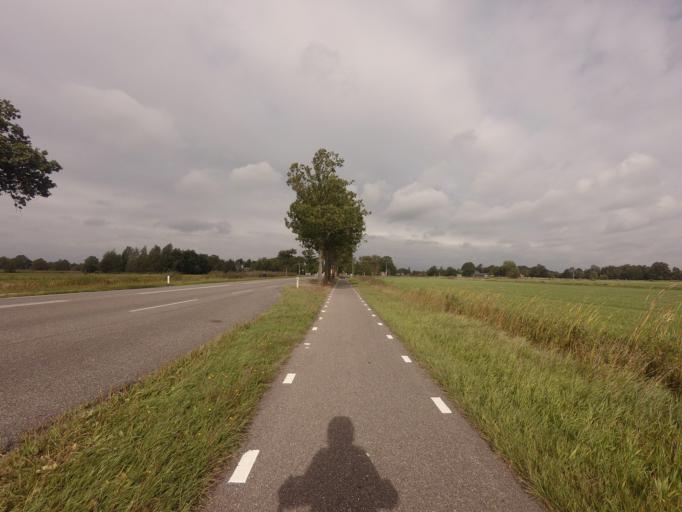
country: NL
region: Friesland
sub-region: Gemeente Opsterland
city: Gorredijk
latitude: 52.9926
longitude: 6.0816
